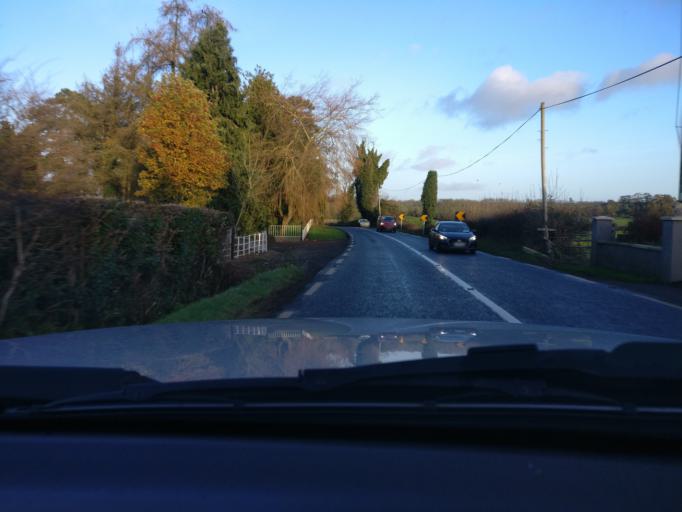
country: IE
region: Ulster
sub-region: An Cabhan
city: Kingscourt
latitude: 53.7921
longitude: -6.7234
